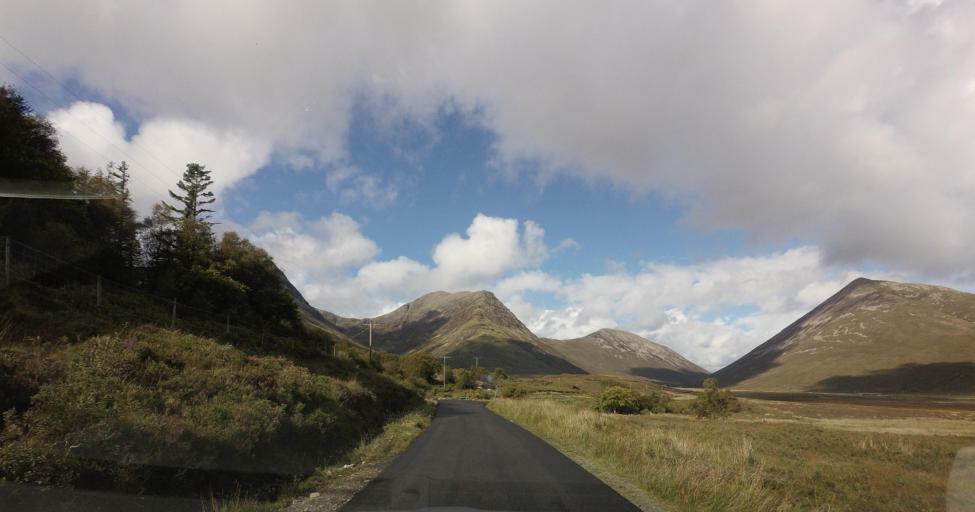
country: GB
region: Scotland
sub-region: Highland
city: Portree
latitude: 57.2186
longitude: -6.0405
